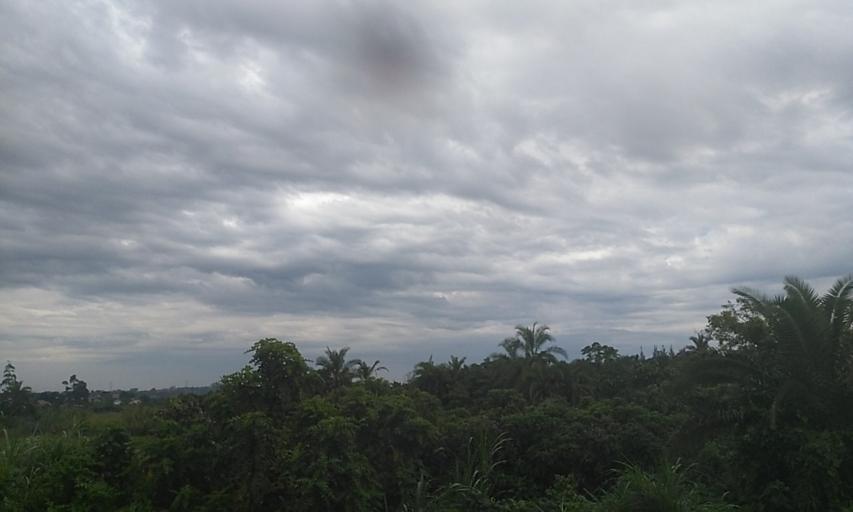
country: UG
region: Central Region
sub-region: Wakiso District
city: Bweyogerere
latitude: 0.3976
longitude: 32.6717
